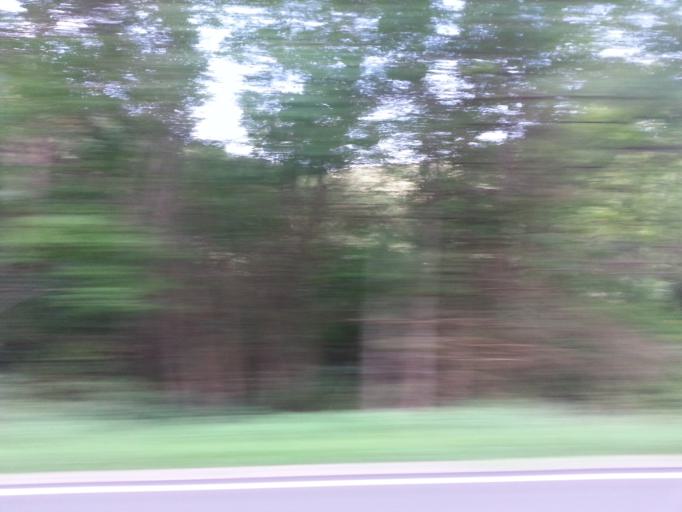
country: US
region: Tennessee
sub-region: Johnson County
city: Mountain City
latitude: 36.6105
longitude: -81.8088
